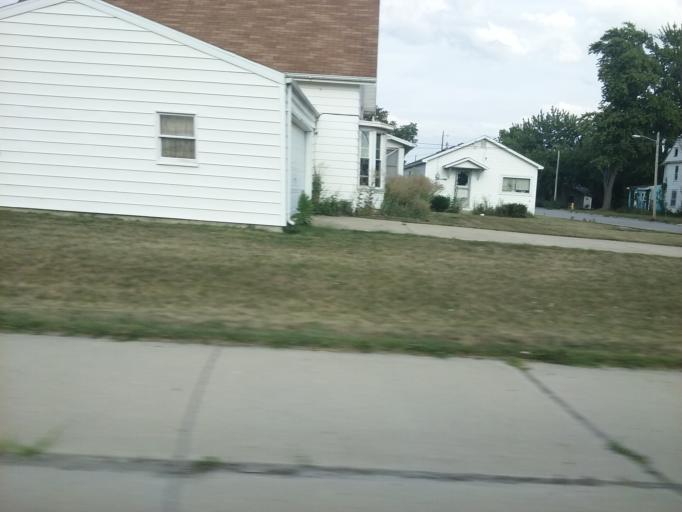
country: US
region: Ohio
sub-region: Wood County
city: Bowling Green
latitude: 41.3279
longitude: -83.6503
